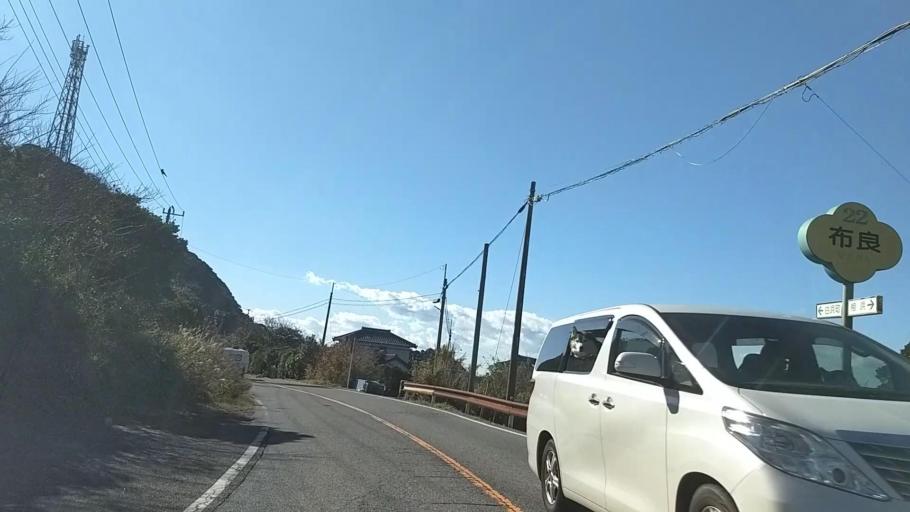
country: JP
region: Chiba
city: Tateyama
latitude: 34.9214
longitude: 139.8286
